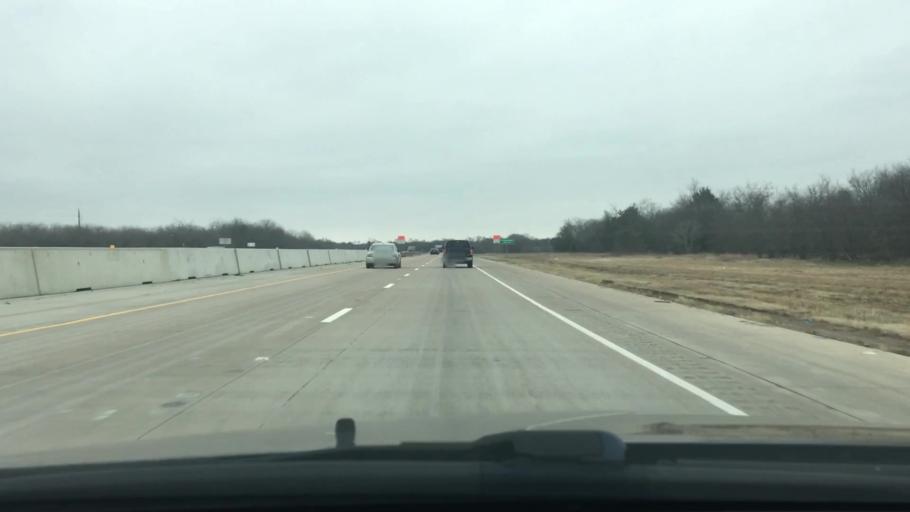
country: US
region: Texas
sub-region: Freestone County
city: Wortham
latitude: 31.8745
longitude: -96.3404
